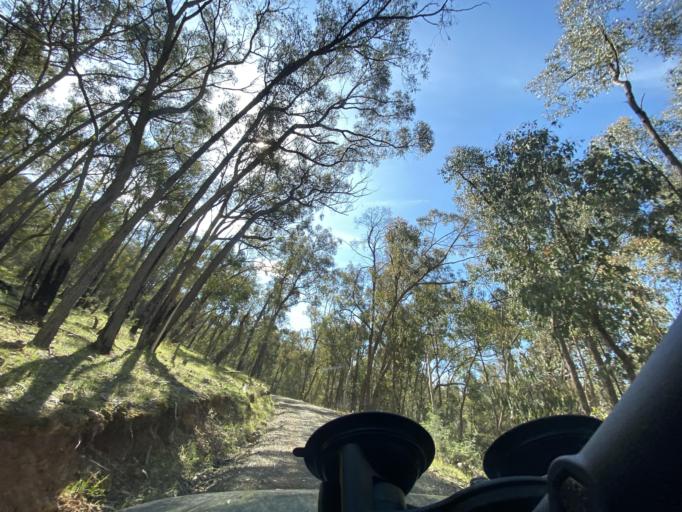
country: AU
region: Victoria
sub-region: Mansfield
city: Mansfield
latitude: -36.8008
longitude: 146.1164
